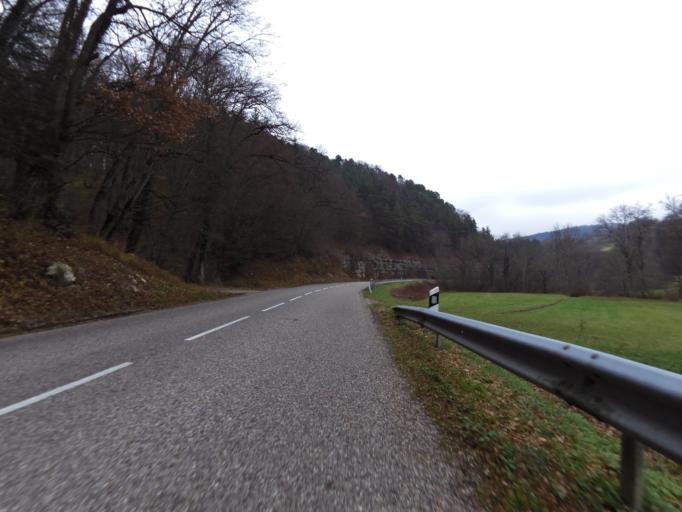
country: FR
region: Alsace
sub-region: Departement du Haut-Rhin
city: Ferrette
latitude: 47.4385
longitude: 7.3433
